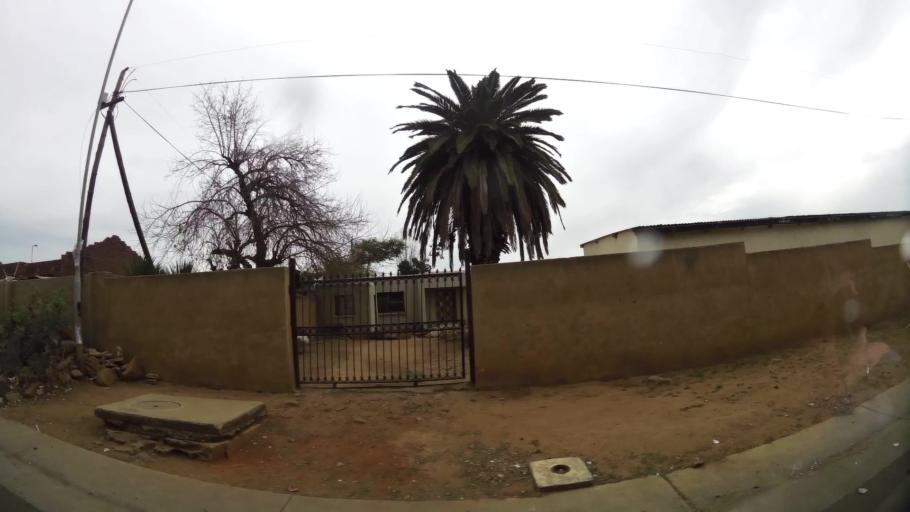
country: ZA
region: Gauteng
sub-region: City of Tshwane Metropolitan Municipality
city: Pretoria
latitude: -25.7093
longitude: 28.3497
